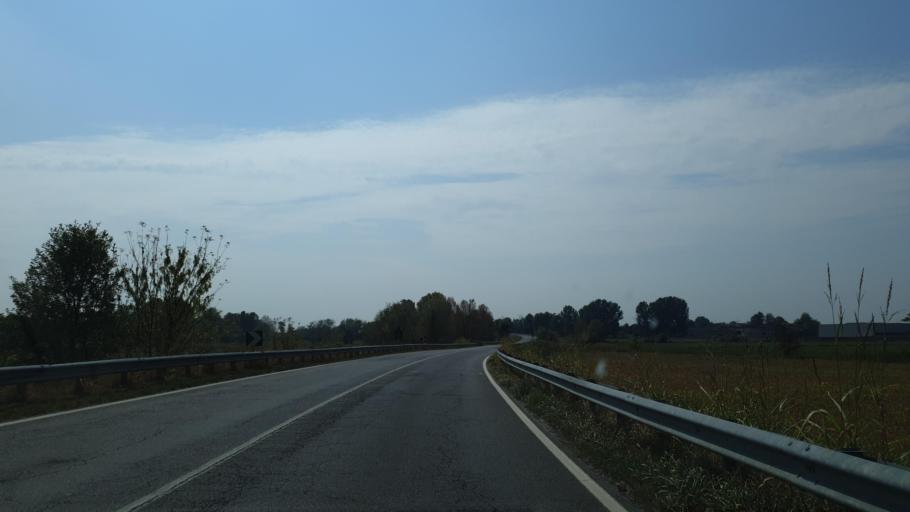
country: IT
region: Lombardy
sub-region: Provincia di Brescia
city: Seniga
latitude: 45.2288
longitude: 10.1842
